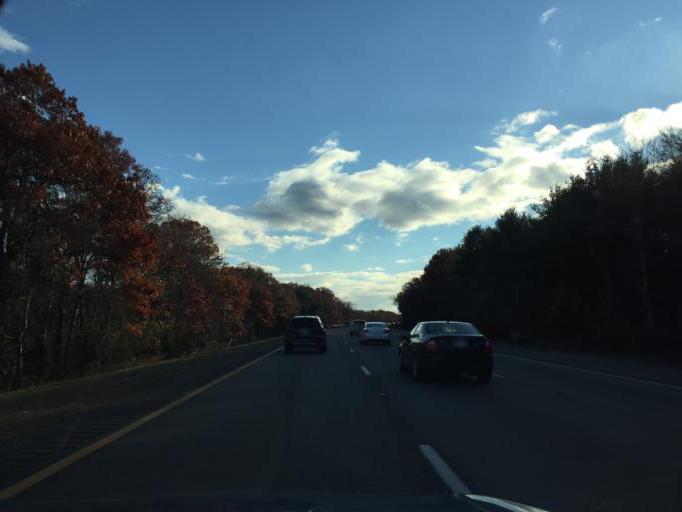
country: US
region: Massachusetts
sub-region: Norfolk County
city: Foxborough
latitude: 42.0817
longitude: -71.2222
